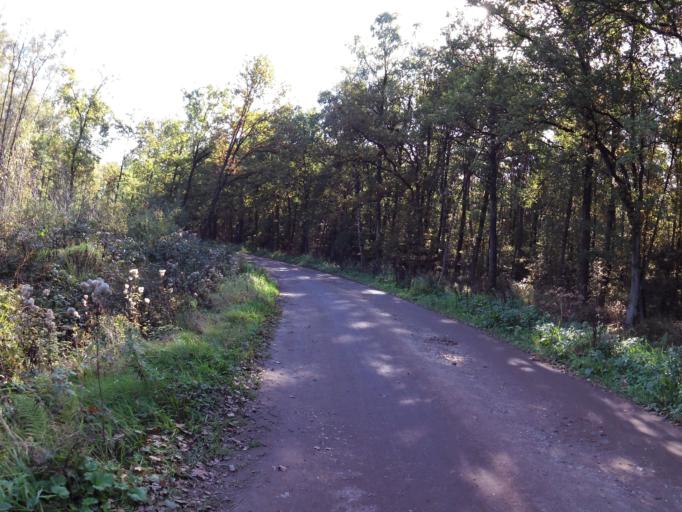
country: NL
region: Limburg
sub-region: Gemeente Weert
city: Weert
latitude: 51.3010
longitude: 5.6760
